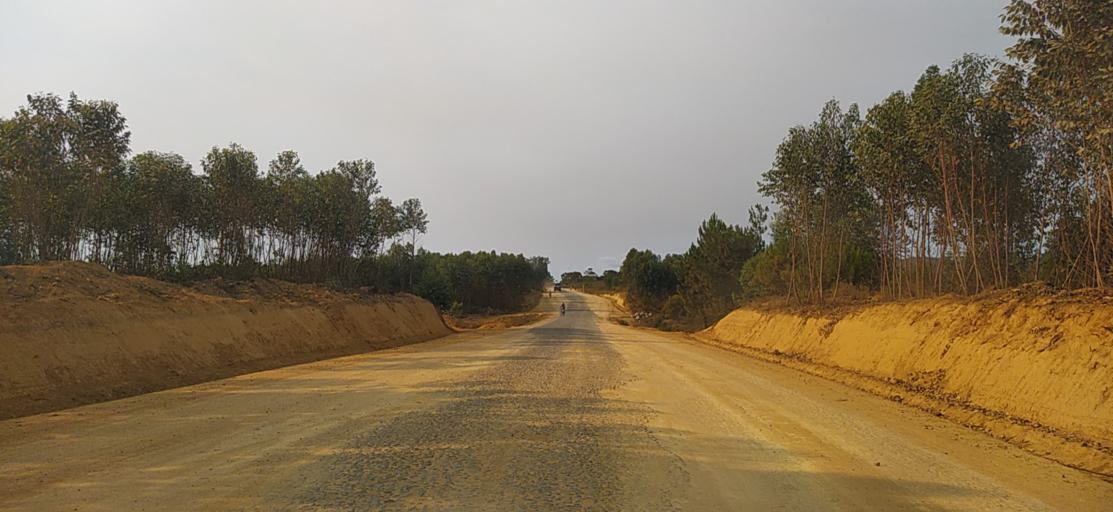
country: MG
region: Alaotra Mangoro
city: Moramanga
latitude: -18.6408
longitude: 48.2756
